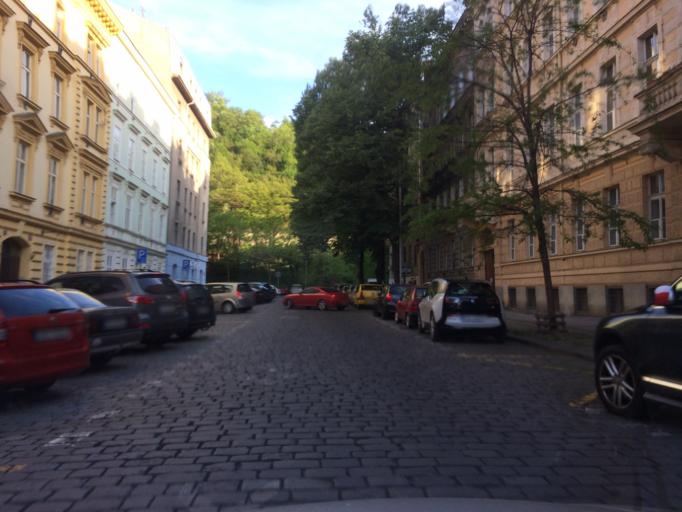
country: CZ
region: Praha
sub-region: Praha 8
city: Karlin
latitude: 50.0903
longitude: 14.4458
